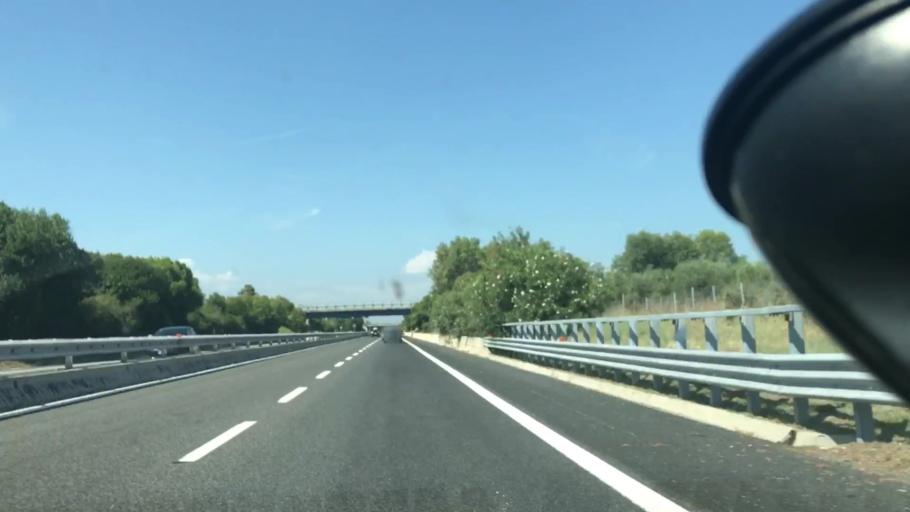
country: IT
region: Abruzzo
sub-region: Provincia di Chieti
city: Ortona
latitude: 42.3352
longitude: 14.3687
